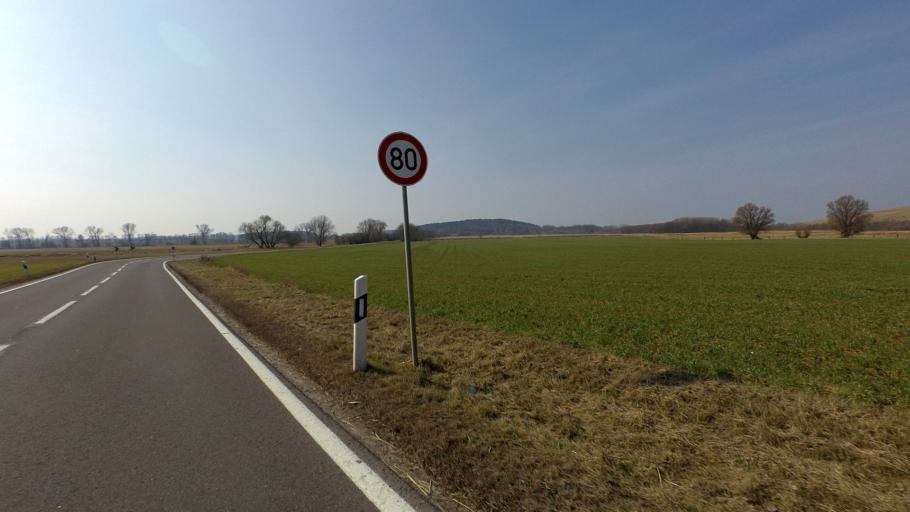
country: DE
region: Brandenburg
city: Gross Kreutz
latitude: 52.4484
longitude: 12.8031
